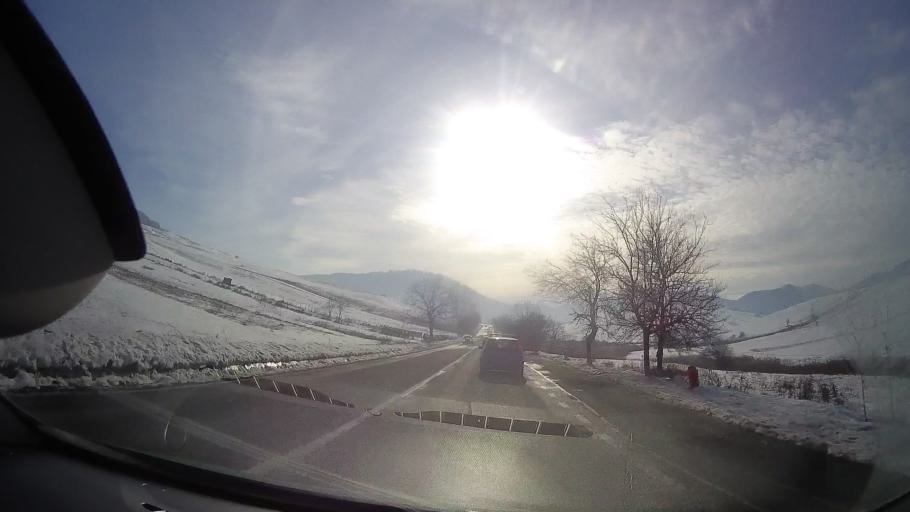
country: RO
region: Neamt
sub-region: Comuna Garcina
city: Garcina
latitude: 46.9870
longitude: 26.3602
